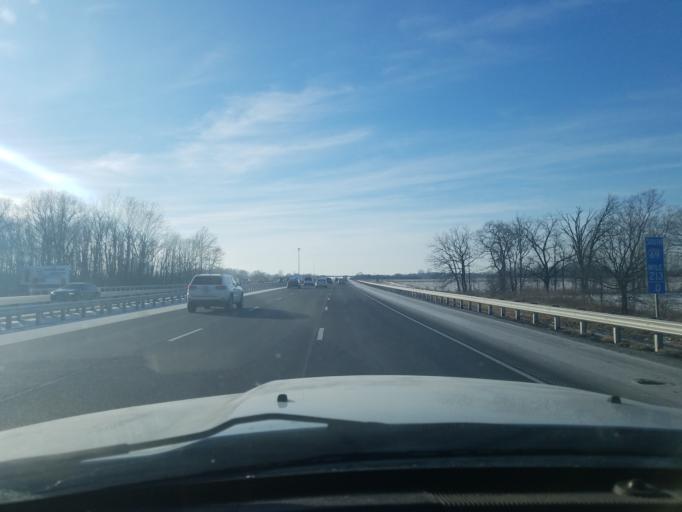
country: US
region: Indiana
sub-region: Hancock County
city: Fortville
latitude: 39.9917
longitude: -85.8703
